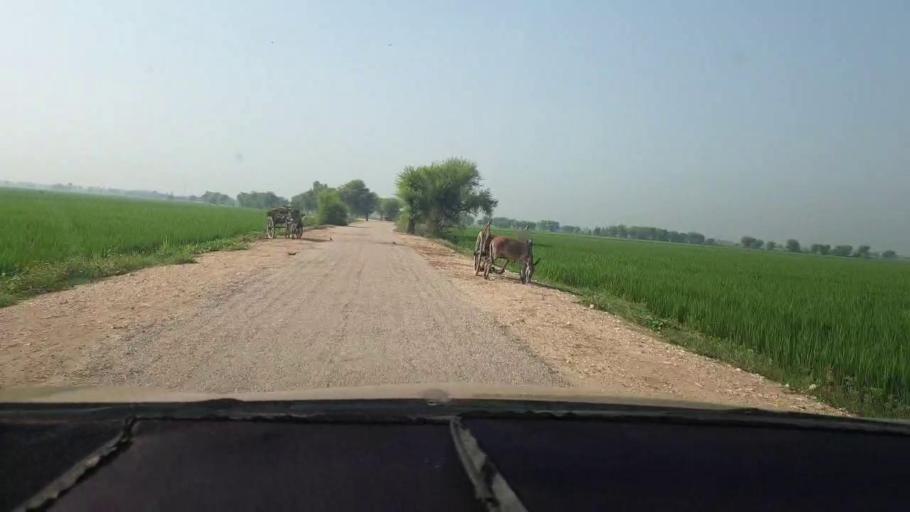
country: PK
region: Sindh
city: Kambar
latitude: 27.6272
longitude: 68.0894
